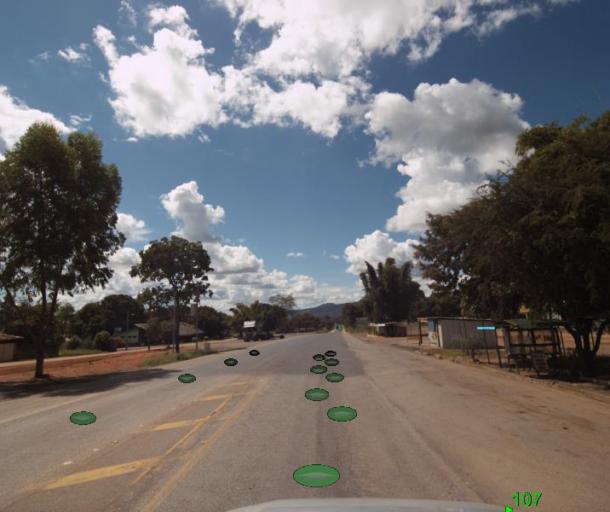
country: BR
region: Goias
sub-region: Porangatu
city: Porangatu
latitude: -13.7126
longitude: -49.0210
